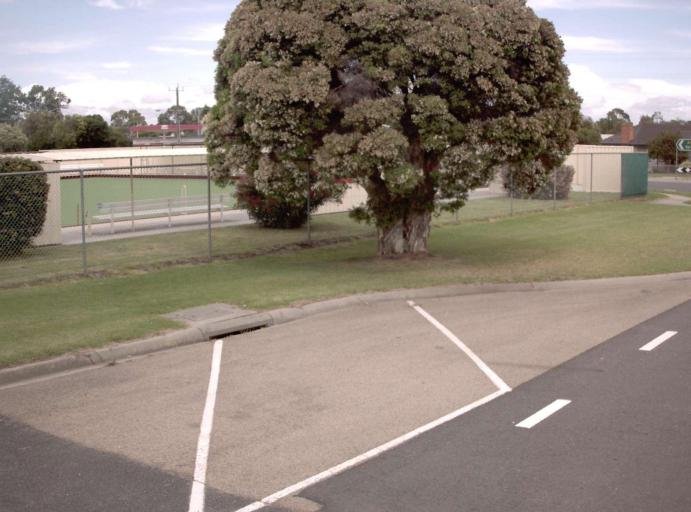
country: AU
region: Victoria
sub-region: Wellington
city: Sale
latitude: -37.9639
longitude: 147.0811
